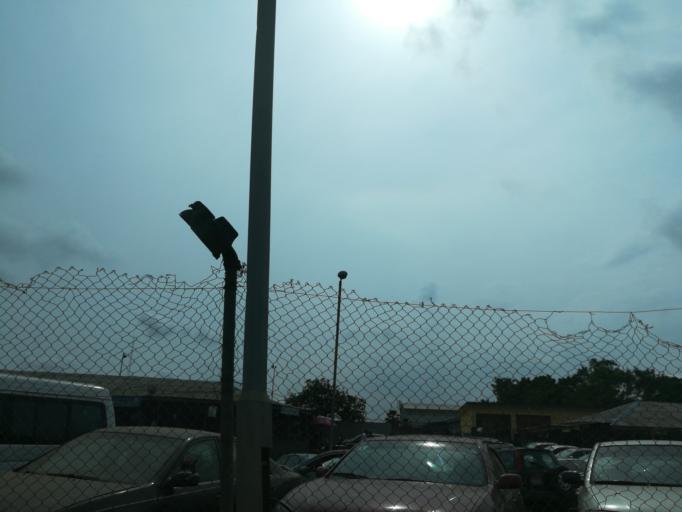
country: NG
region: Lagos
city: Oshodi
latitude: 6.5748
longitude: 3.3234
